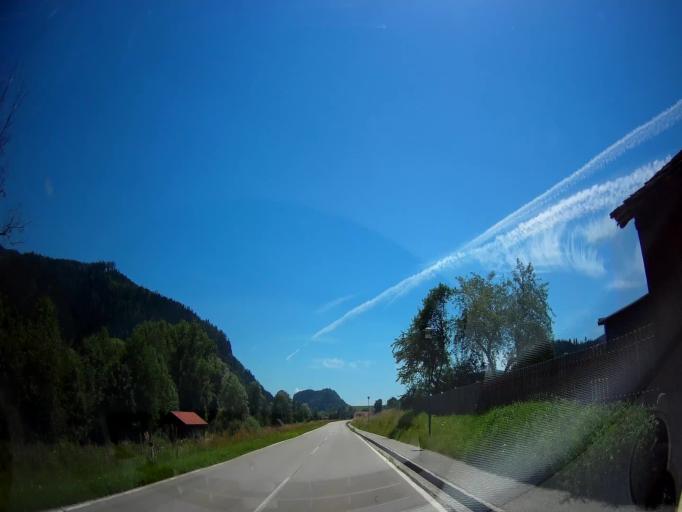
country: AT
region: Carinthia
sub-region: Politischer Bezirk Sankt Veit an der Glan
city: Micheldorf
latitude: 46.9083
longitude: 14.4341
